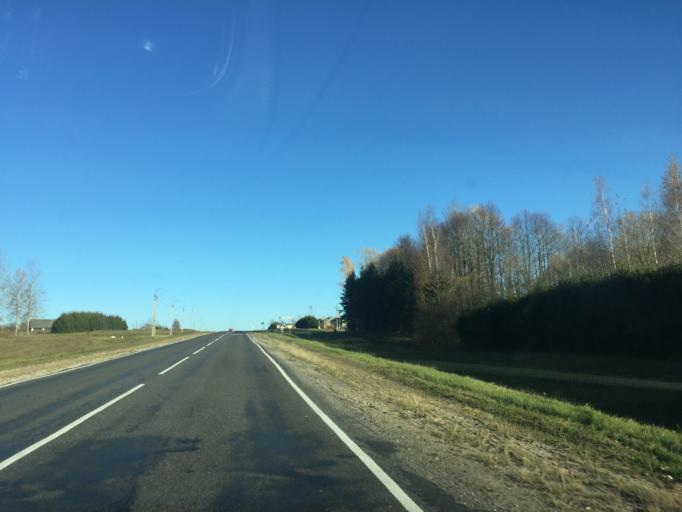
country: BY
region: Vitebsk
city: Dzisna
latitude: 55.3507
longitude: 28.3161
